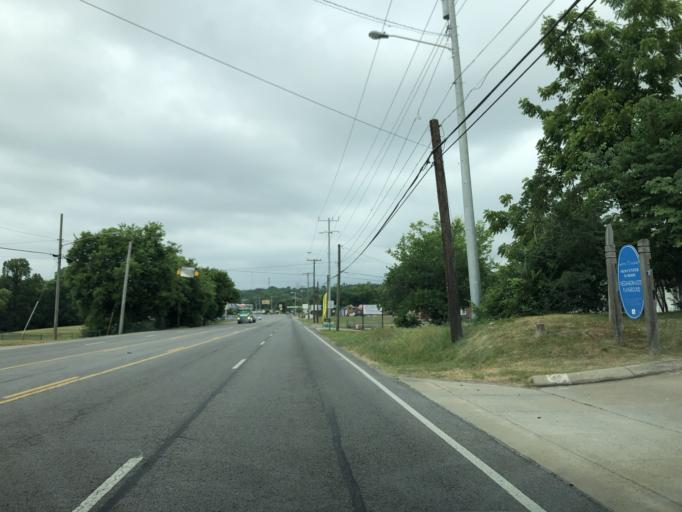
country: US
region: Tennessee
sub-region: Davidson County
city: Goodlettsville
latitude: 36.2906
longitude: -86.7383
